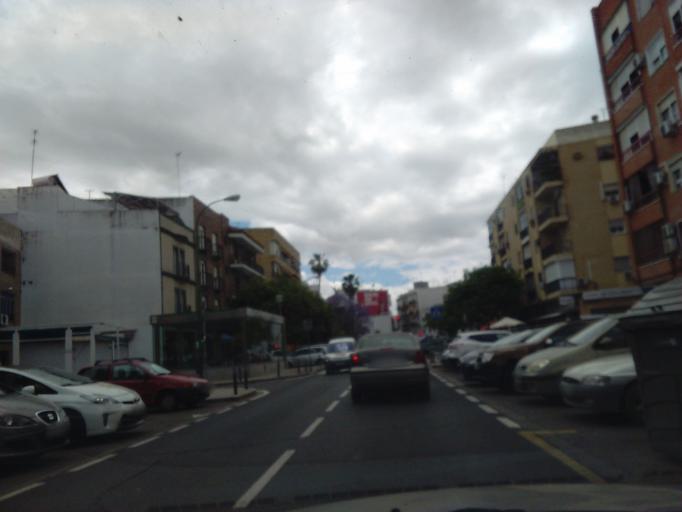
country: ES
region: Andalusia
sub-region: Provincia de Sevilla
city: Sevilla
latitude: 37.3719
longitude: -5.9520
